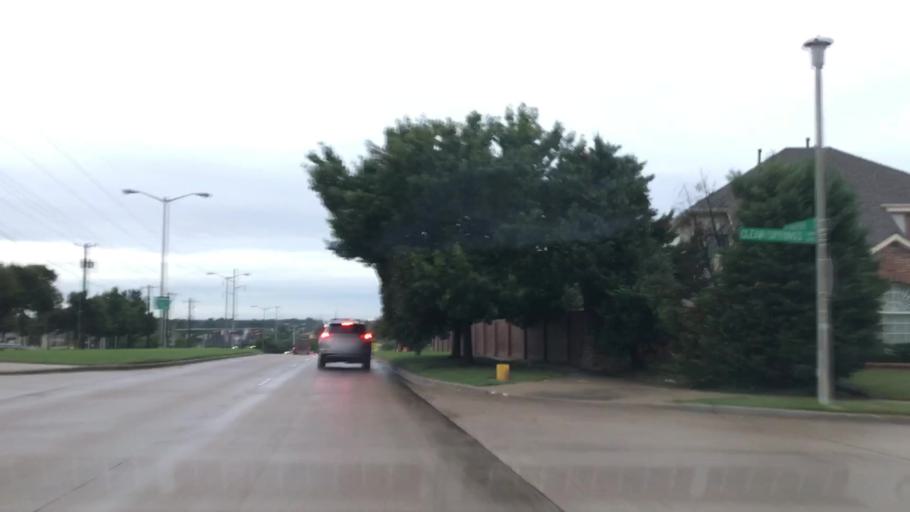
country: US
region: Texas
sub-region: Collin County
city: Plano
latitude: 32.9768
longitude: -96.6655
